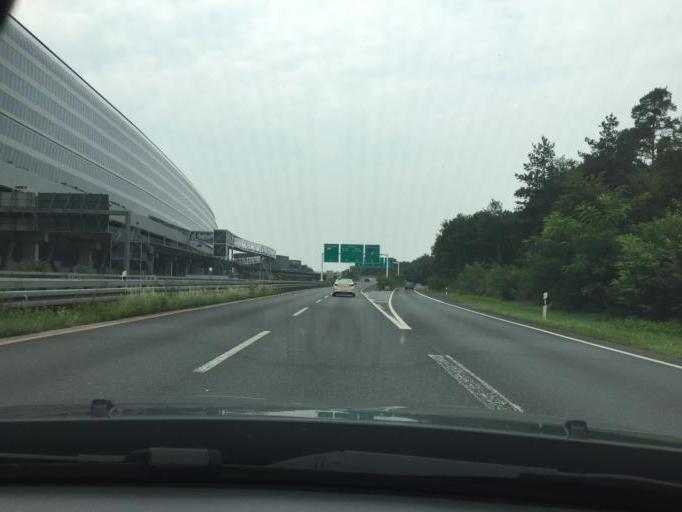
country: DE
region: Hesse
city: Kelsterbach
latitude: 50.0535
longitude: 8.5693
